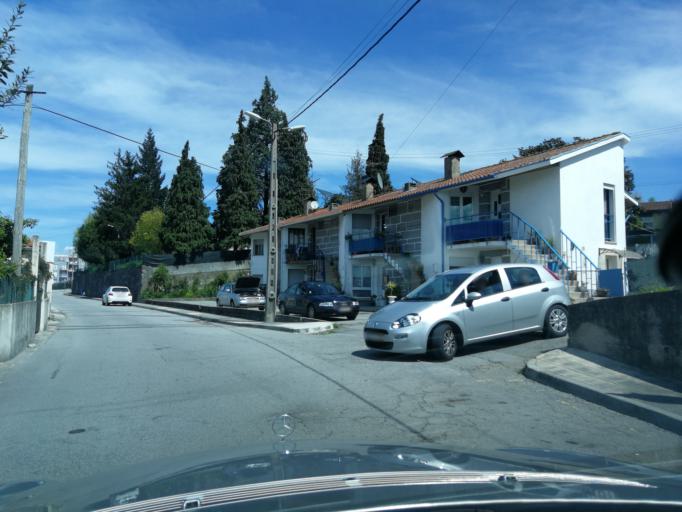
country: PT
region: Braga
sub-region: Vila Nova de Famalicao
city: Vila Nova de Famalicao
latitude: 41.4154
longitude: -8.5155
